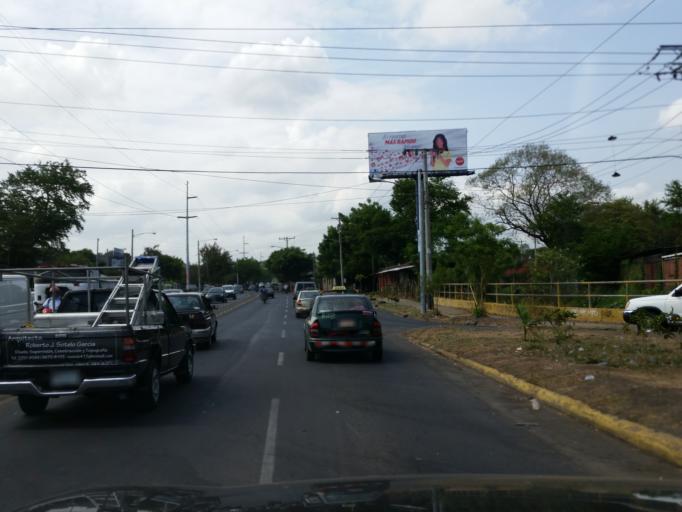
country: NI
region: Managua
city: Managua
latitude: 12.1246
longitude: -86.2748
